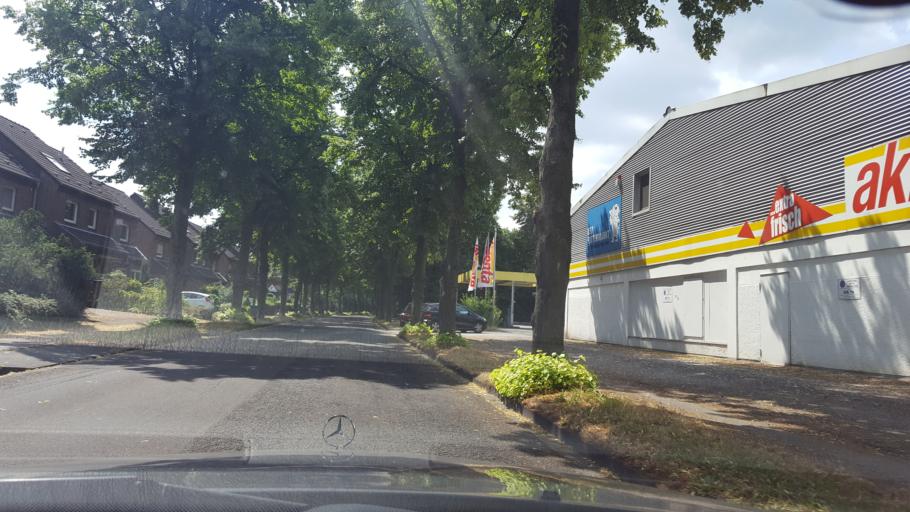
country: DE
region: North Rhine-Westphalia
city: Marl
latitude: 51.6644
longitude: 7.1502
